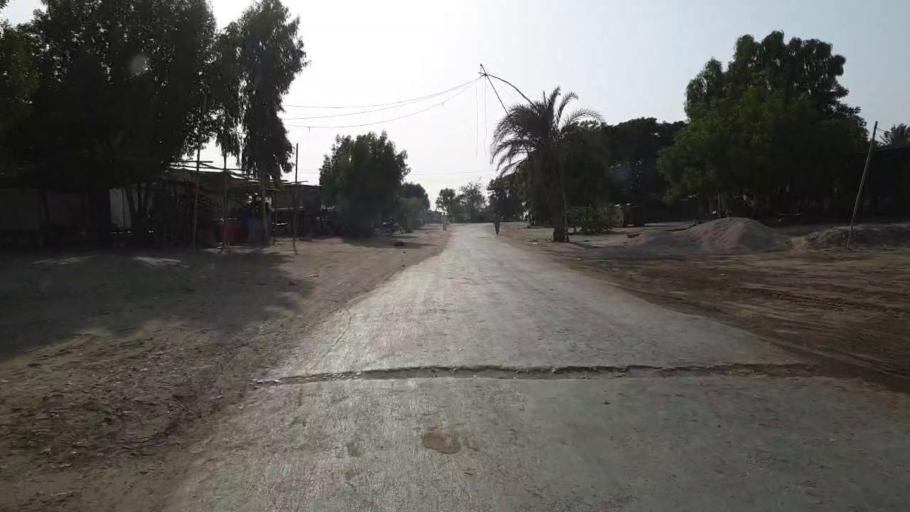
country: PK
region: Sindh
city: Jam Sahib
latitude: 26.3808
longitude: 68.8871
